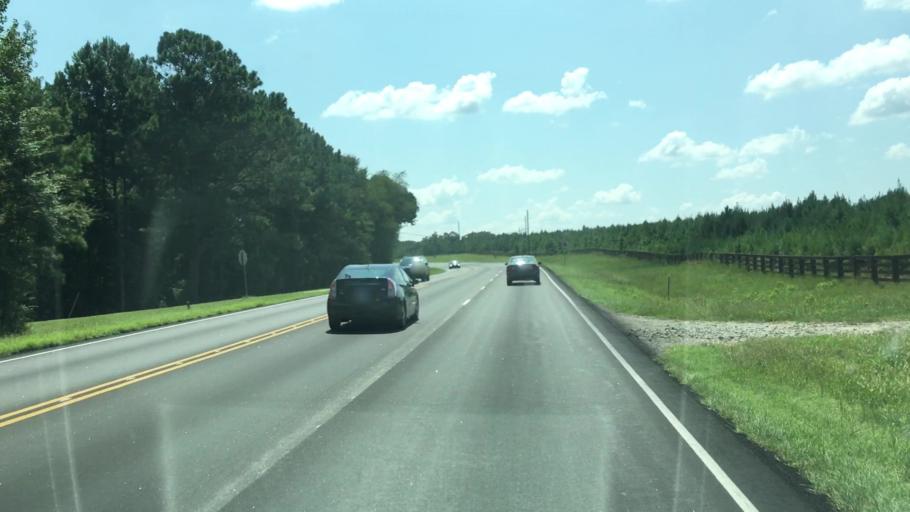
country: US
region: Georgia
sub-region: Morgan County
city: Madison
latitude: 33.7136
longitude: -83.4395
